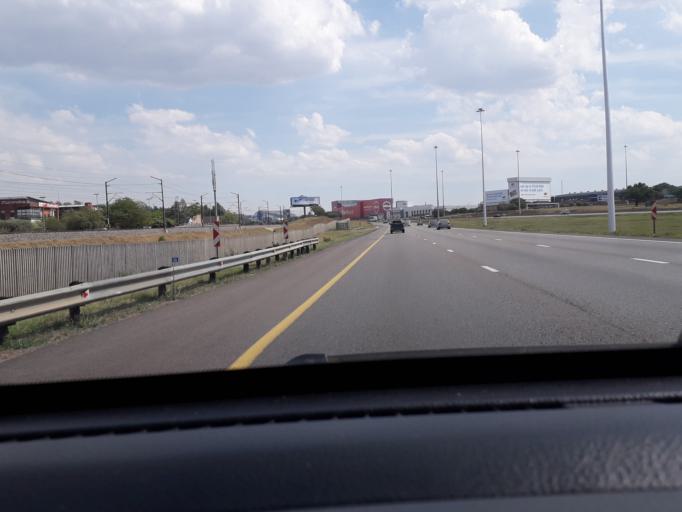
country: ZA
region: Gauteng
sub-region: City of Tshwane Metropolitan Municipality
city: Centurion
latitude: -25.8789
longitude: 28.1704
